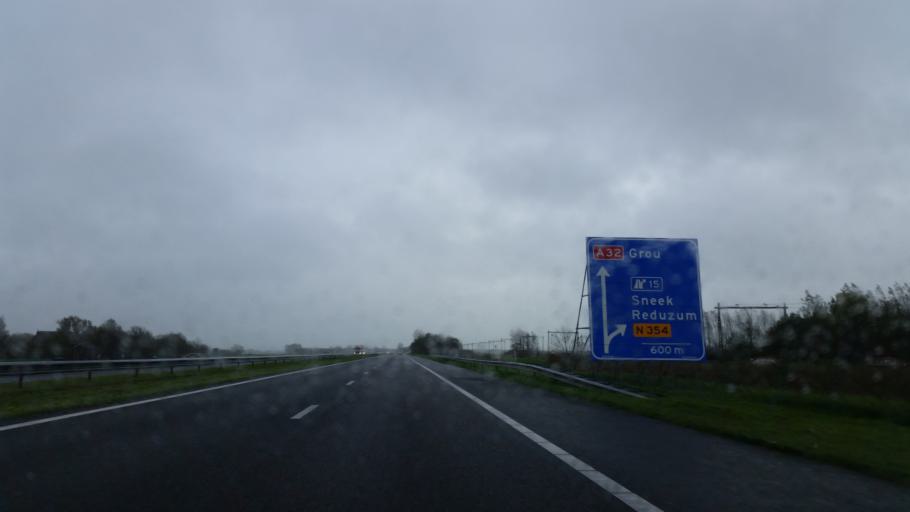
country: NL
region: Friesland
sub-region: Gemeente Boarnsterhim
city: Reduzum
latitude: 53.1247
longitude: 5.8059
